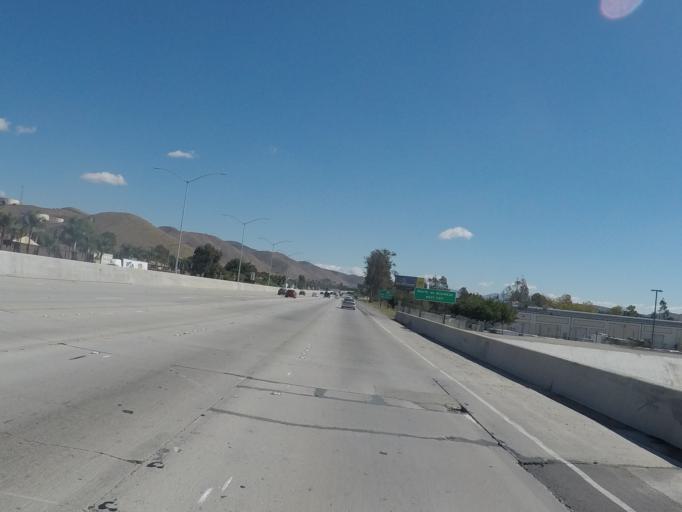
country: US
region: California
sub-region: Riverside County
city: Mira Loma
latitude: 34.0184
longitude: -117.5138
